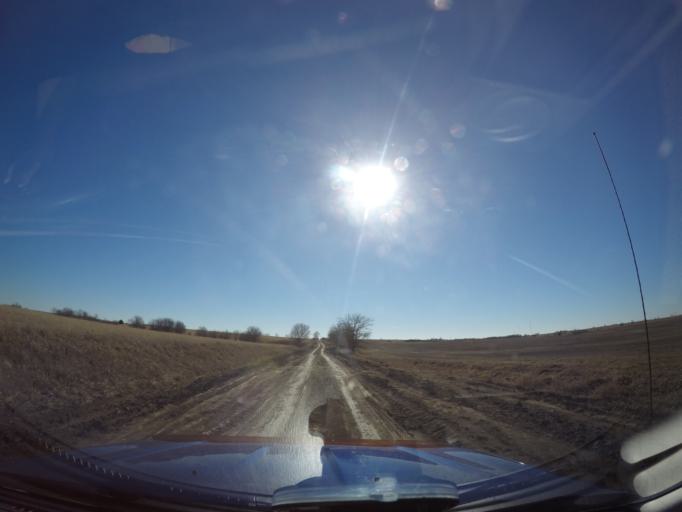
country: US
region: Kansas
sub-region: Dickinson County
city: Herington
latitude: 38.6958
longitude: -96.8935
